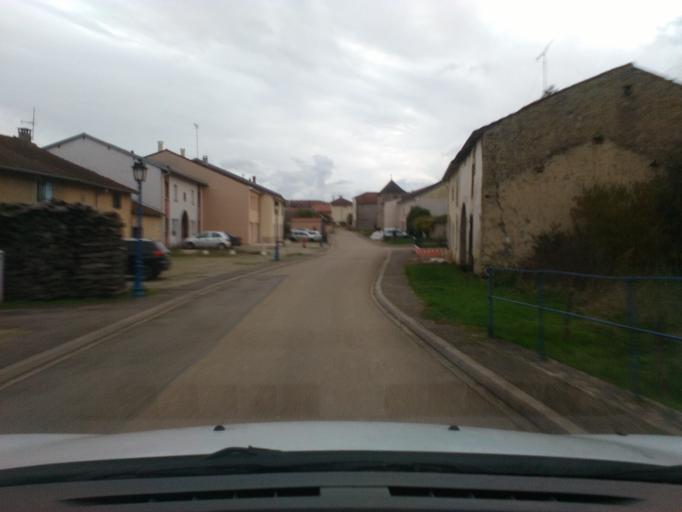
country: FR
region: Lorraine
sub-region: Departement des Vosges
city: Mirecourt
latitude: 48.3332
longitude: 6.0589
